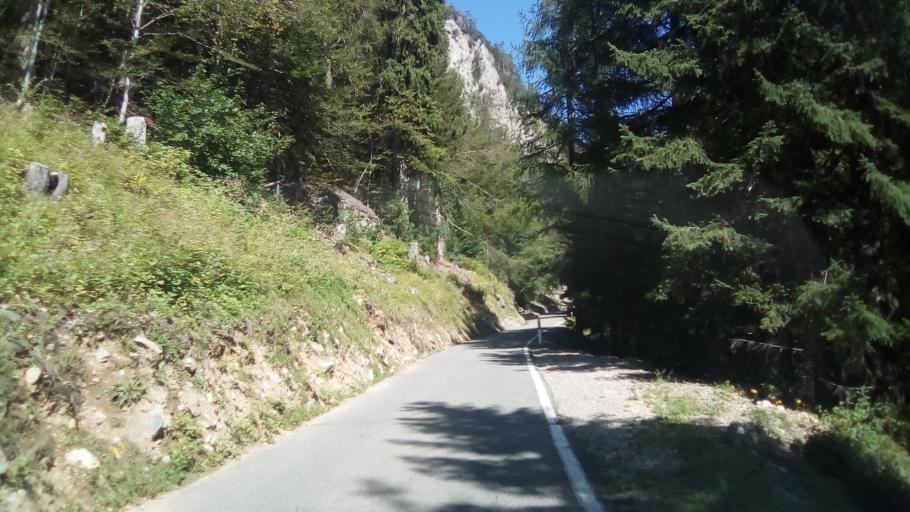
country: CH
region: Valais
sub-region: Saint-Maurice District
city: Salvan
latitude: 46.1327
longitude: 7.0187
